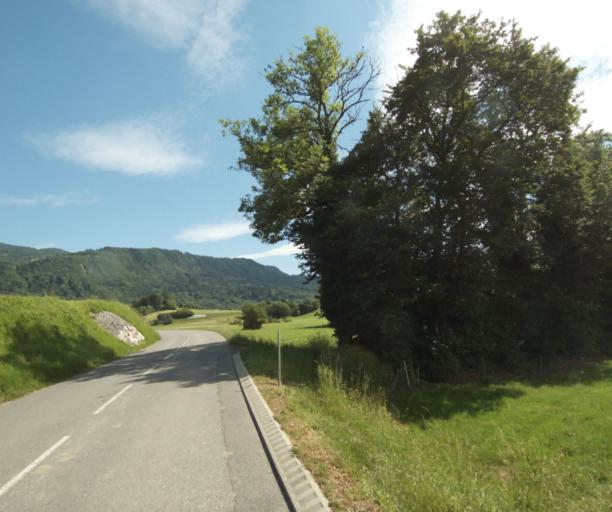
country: FR
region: Rhone-Alpes
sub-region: Departement de la Haute-Savoie
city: Perrignier
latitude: 46.3005
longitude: 6.4492
